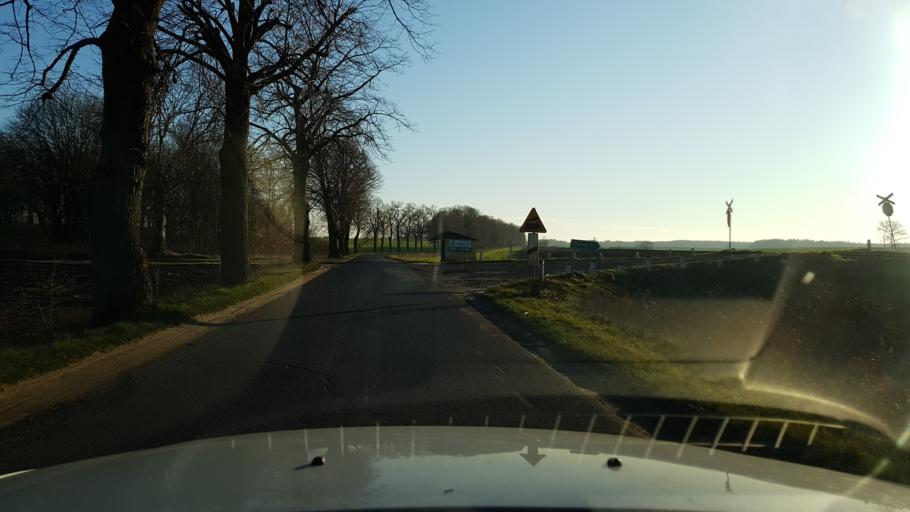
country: PL
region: West Pomeranian Voivodeship
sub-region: Powiat gryficki
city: Trzebiatow
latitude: 54.0255
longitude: 15.2817
